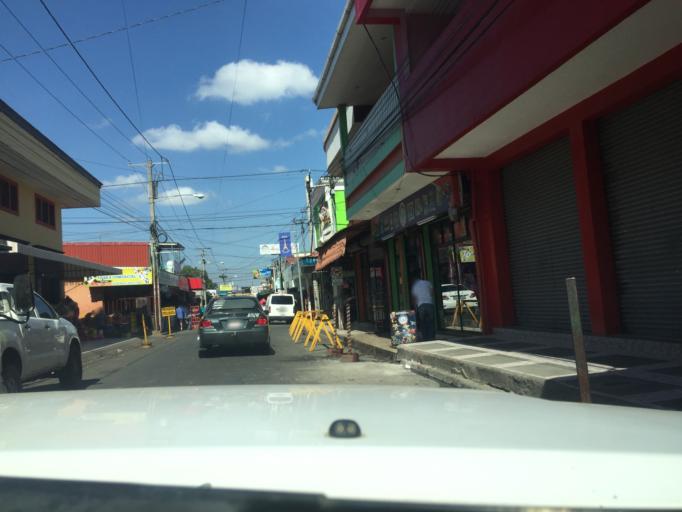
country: NI
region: Managua
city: Managua
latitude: 12.1491
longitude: -86.2563
